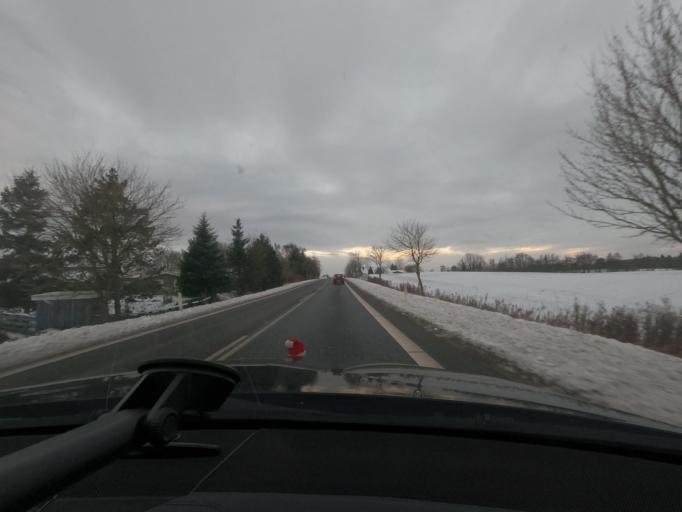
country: DE
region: Schleswig-Holstein
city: Wees
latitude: 54.8788
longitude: 9.4735
